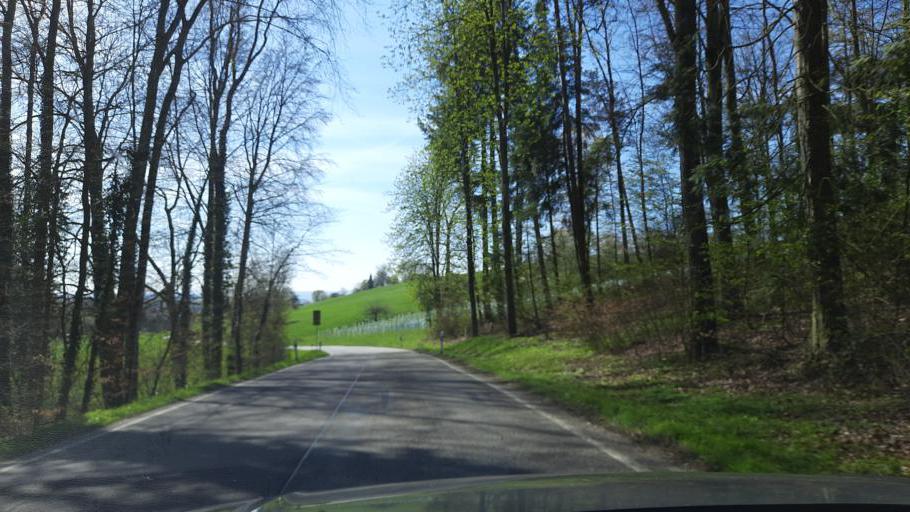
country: DE
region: Baden-Wuerttemberg
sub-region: Regierungsbezirk Stuttgart
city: Widdern
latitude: 49.2720
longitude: 9.3920
